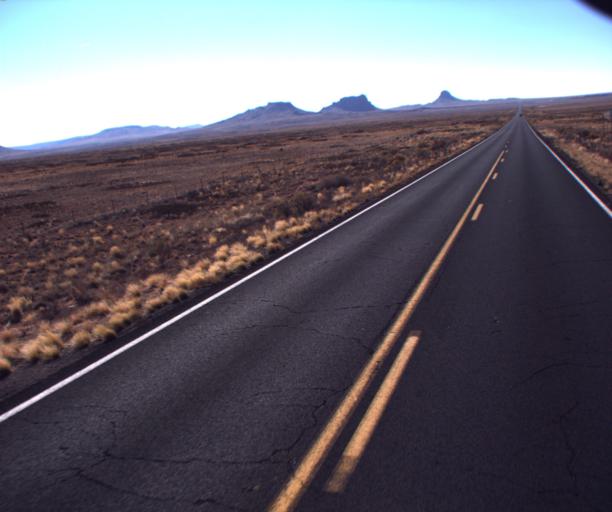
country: US
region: Arizona
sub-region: Navajo County
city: Dilkon
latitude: 35.3911
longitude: -110.4258
